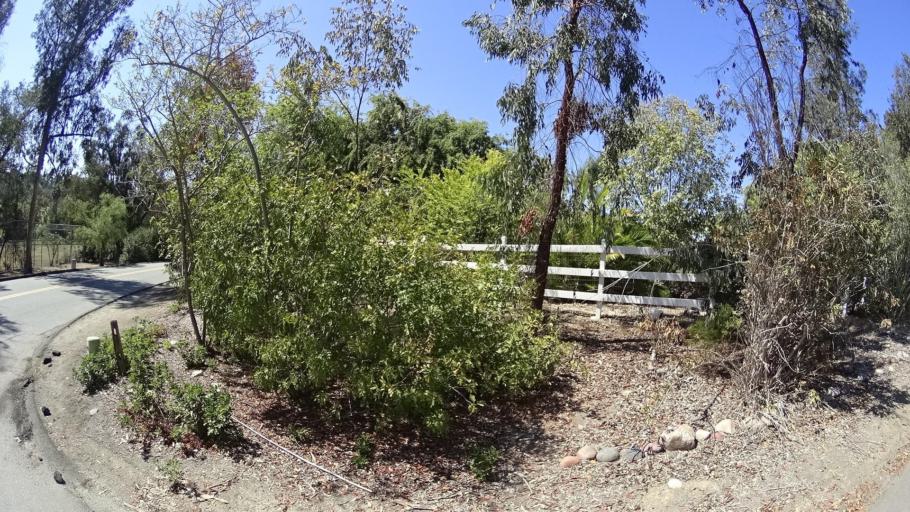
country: US
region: California
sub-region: San Diego County
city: Rancho Santa Fe
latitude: 33.0251
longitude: -117.2122
